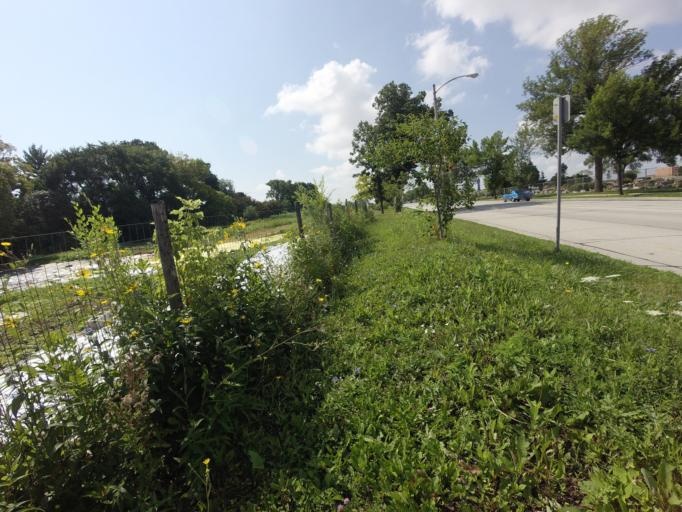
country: US
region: Wisconsin
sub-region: Milwaukee County
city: Saint Francis
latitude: 42.9757
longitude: -87.9192
